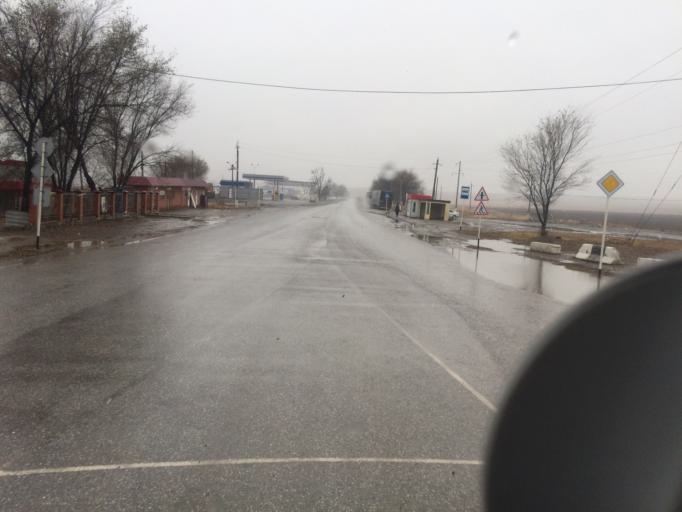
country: KG
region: Chuy
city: Kant
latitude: 43.0012
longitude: 74.8668
